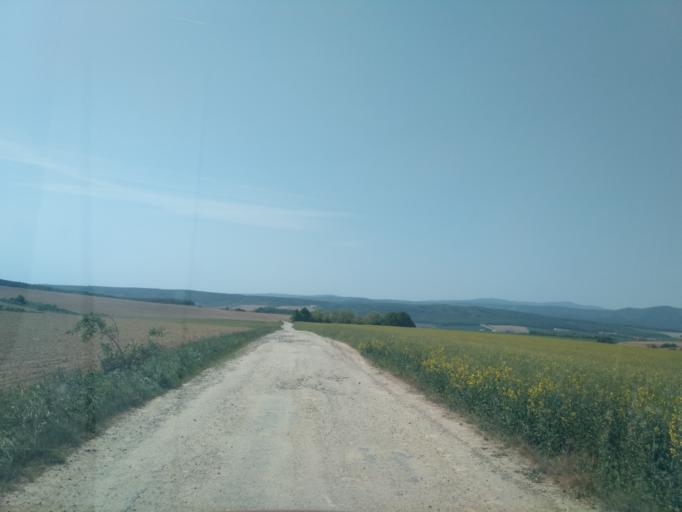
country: SK
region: Kosicky
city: Kosice
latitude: 48.7935
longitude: 21.3720
